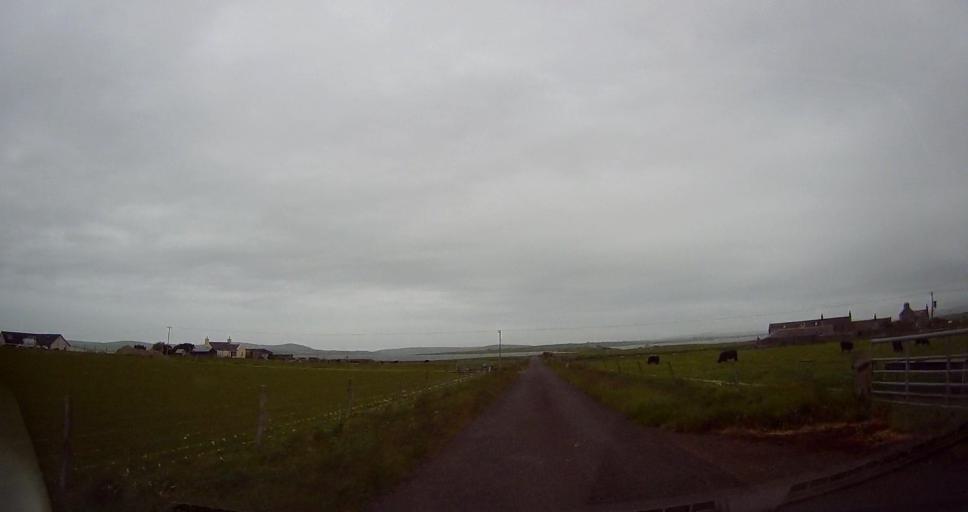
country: GB
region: Scotland
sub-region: Orkney Islands
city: Stromness
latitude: 58.9883
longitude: -3.1967
